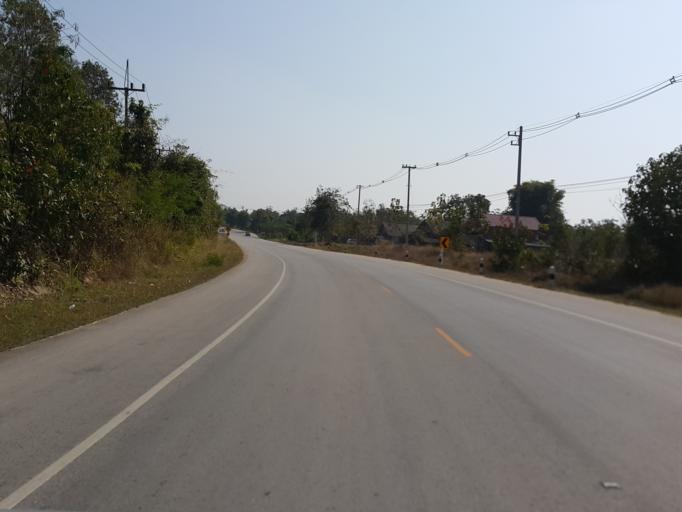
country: TH
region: Lampang
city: Chae Hom
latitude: 18.7391
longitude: 99.5770
